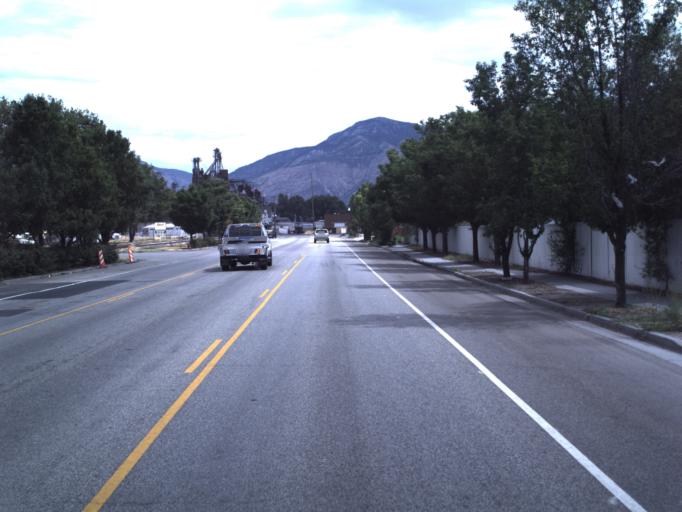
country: US
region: Utah
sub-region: Weber County
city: Ogden
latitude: 41.2213
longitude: -112.0026
